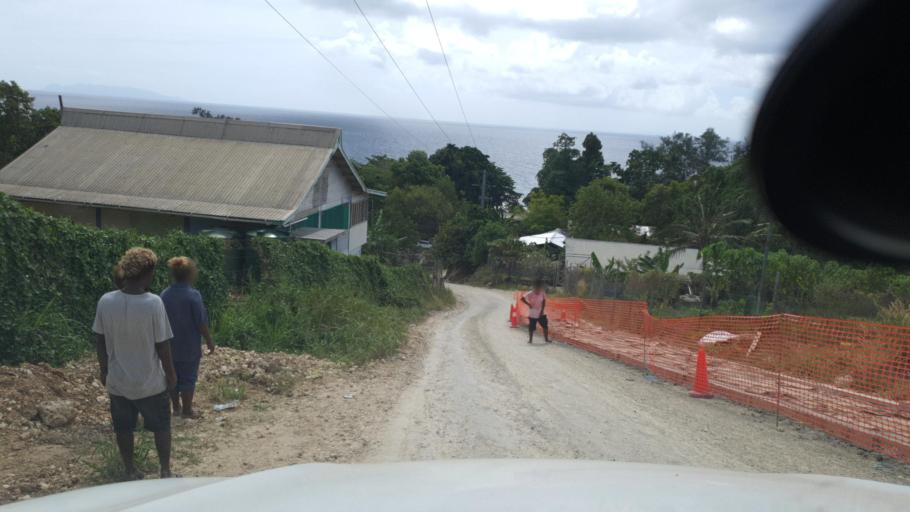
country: SB
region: Guadalcanal
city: Honiara
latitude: -9.4255
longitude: 159.9245
